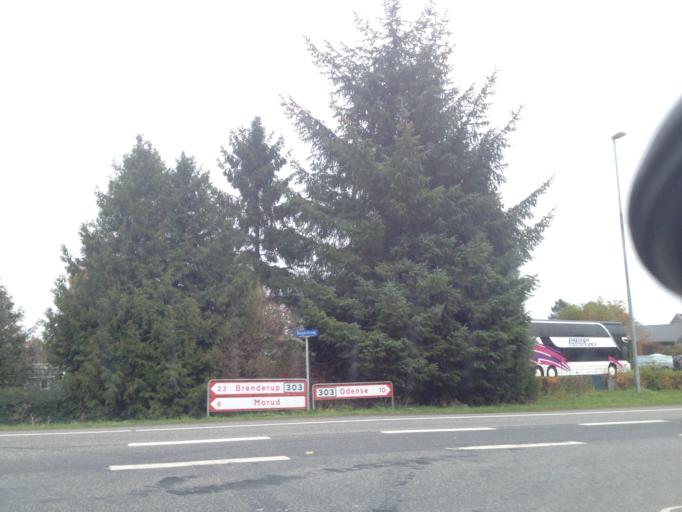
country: DK
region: South Denmark
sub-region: Nordfyns Kommune
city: Sonderso
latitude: 55.4223
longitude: 10.2564
